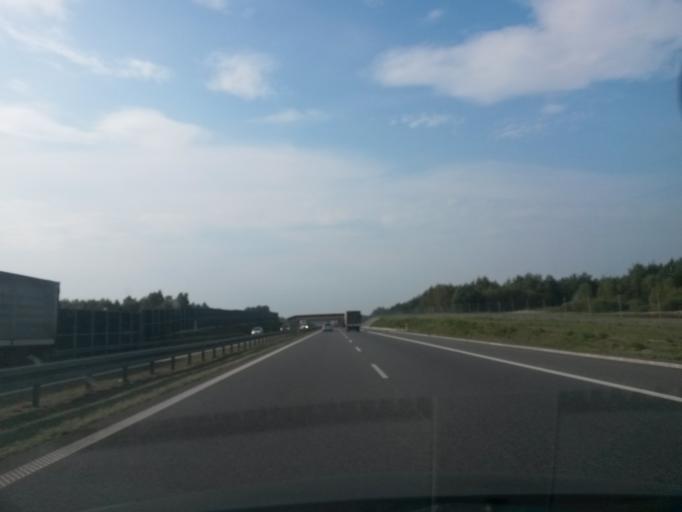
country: PL
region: Lesser Poland Voivodeship
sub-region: Powiat bochenski
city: Jodlowka
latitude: 49.9981
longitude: 20.5576
